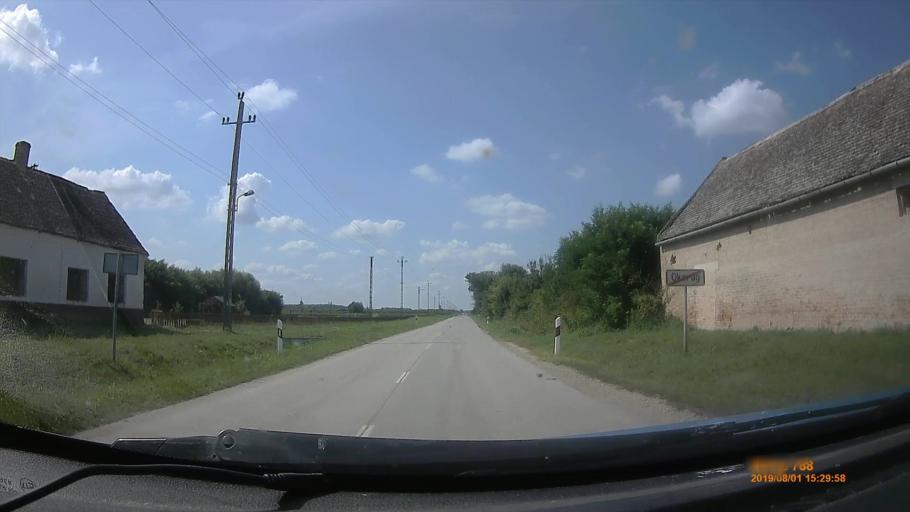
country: HU
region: Baranya
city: Sellye
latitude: 45.9260
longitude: 17.8750
